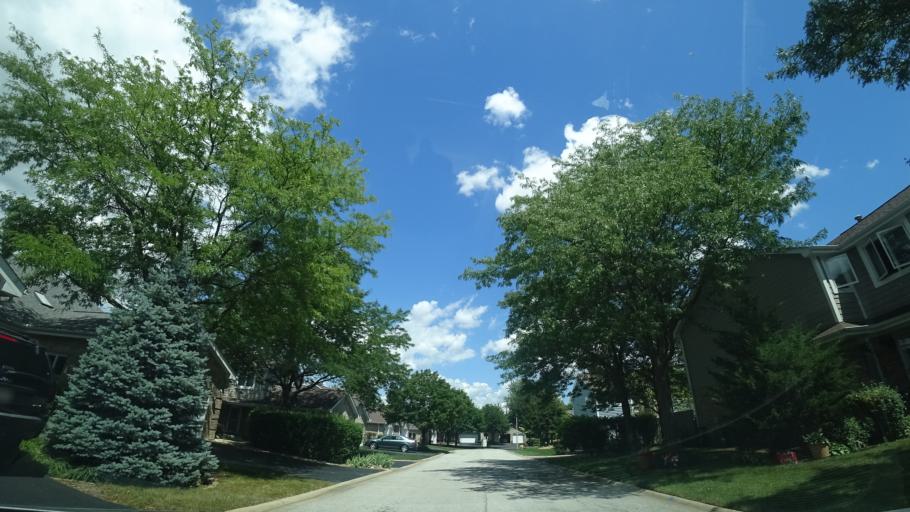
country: US
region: Illinois
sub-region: Will County
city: Homer Glen
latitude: 41.5759
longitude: -87.8958
